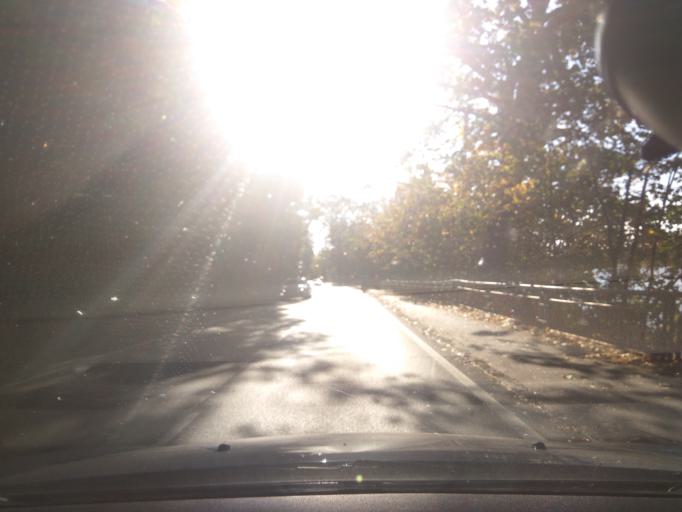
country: SK
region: Trnavsky
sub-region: Okres Trnava
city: Piestany
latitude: 48.5840
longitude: 17.8385
